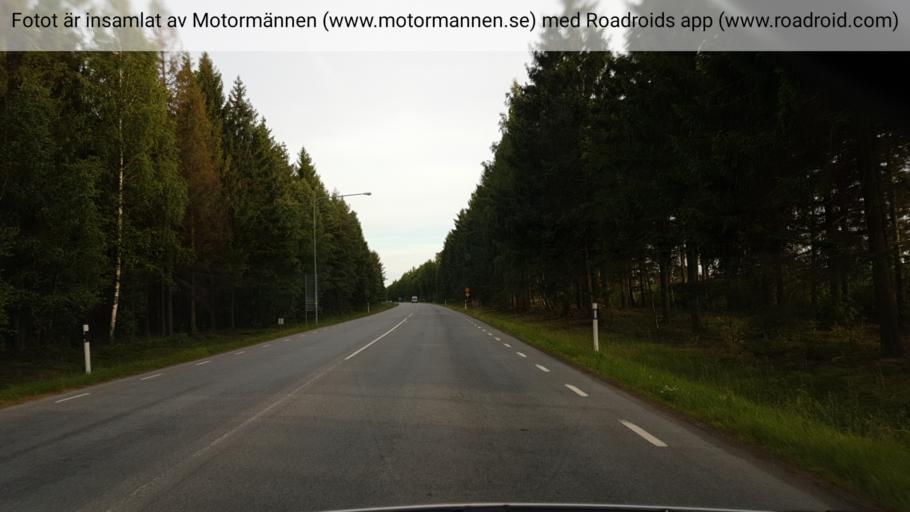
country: SE
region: Vaestra Goetaland
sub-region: Lidkopings Kommun
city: Lidkoping
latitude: 58.5178
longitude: 13.1140
